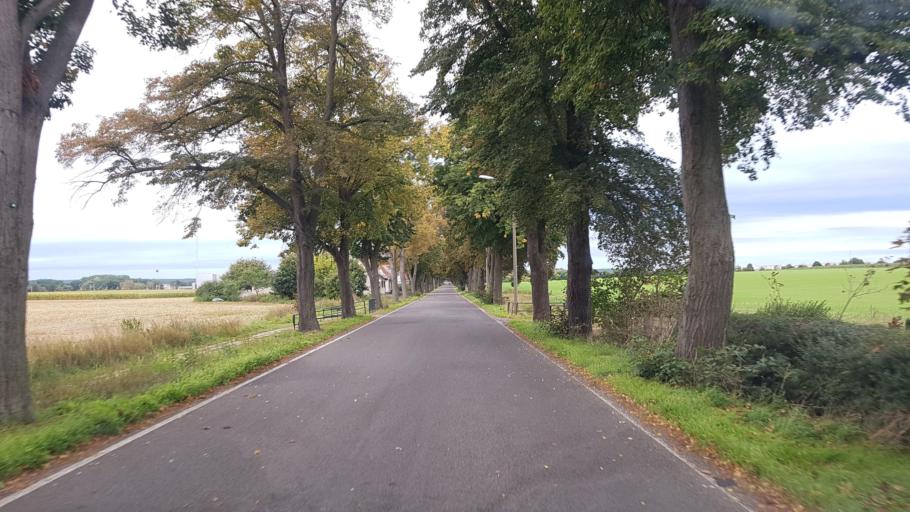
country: DE
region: Brandenburg
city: Golssen
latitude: 51.9730
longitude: 13.5879
